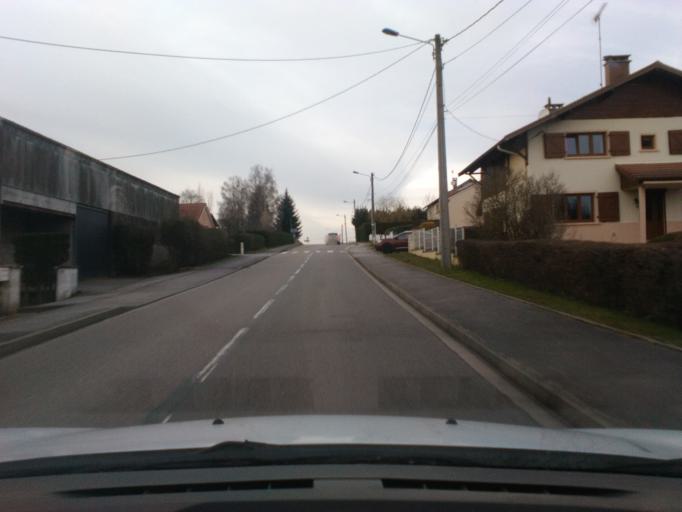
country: FR
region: Lorraine
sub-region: Departement des Vosges
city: Portieux
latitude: 48.3489
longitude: 6.3401
